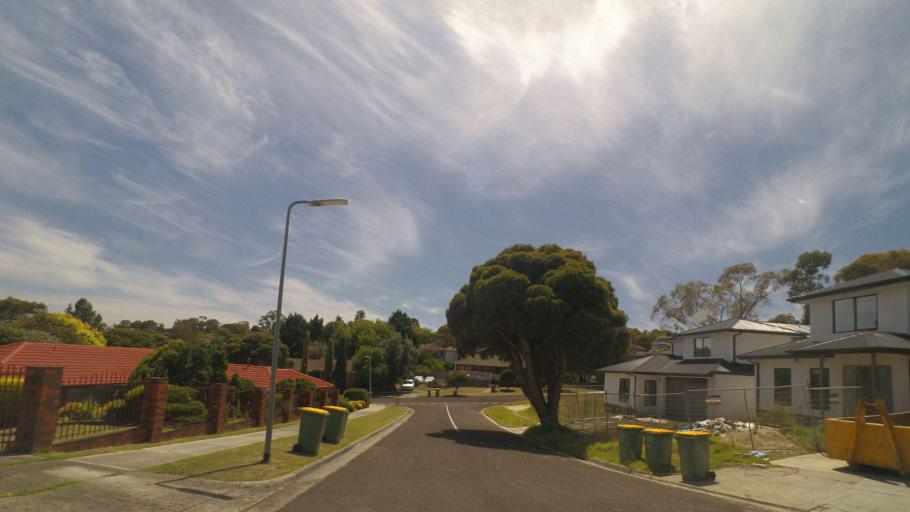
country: AU
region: Victoria
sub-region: Maroondah
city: Croydon North
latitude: -37.7681
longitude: 145.3169
